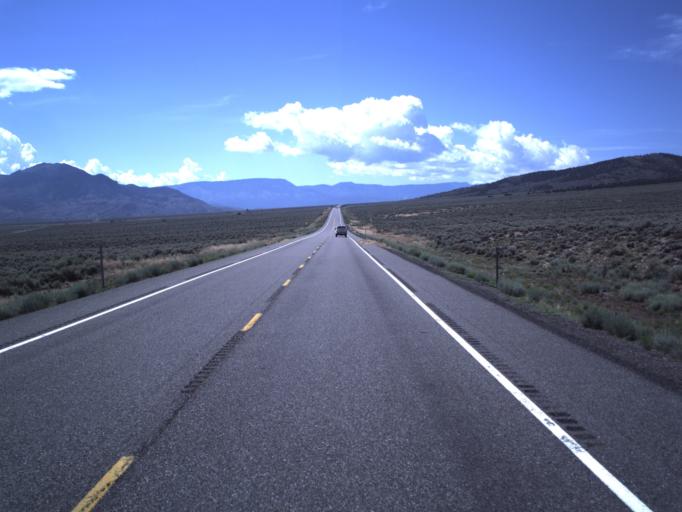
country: US
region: Utah
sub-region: Piute County
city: Junction
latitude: 38.3720
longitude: -112.2258
